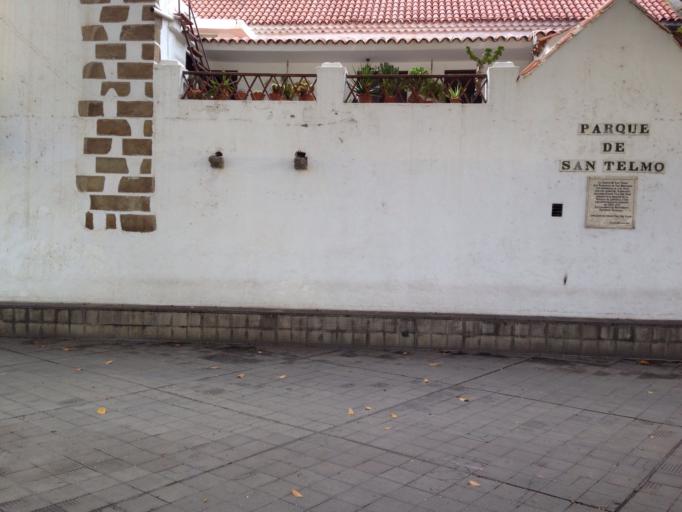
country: ES
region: Canary Islands
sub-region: Provincia de Las Palmas
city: Las Palmas de Gran Canaria
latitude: 28.1084
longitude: -15.4170
